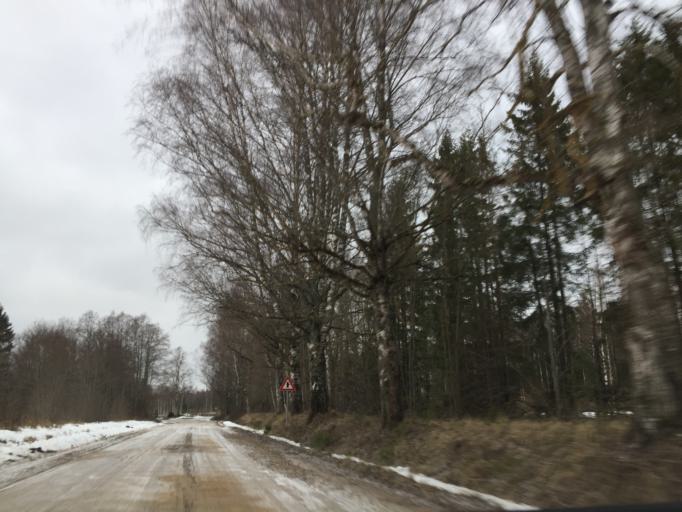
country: LV
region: Salacgrivas
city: Salacgriva
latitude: 57.6522
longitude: 24.4610
